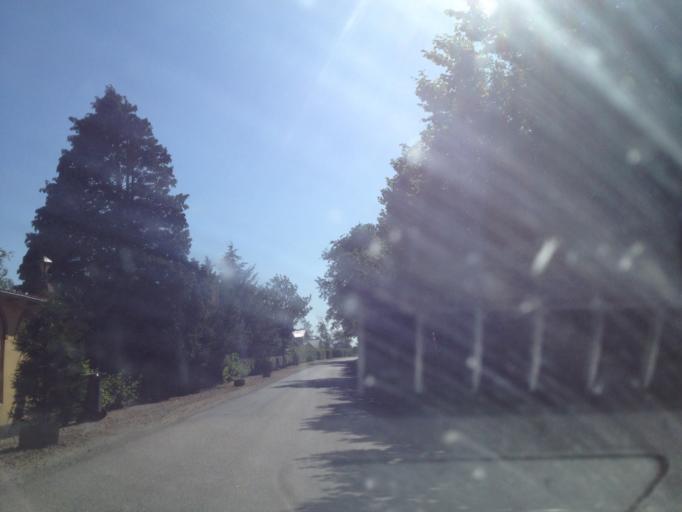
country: DK
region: South Denmark
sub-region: Kolding Kommune
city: Christiansfeld
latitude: 55.4040
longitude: 9.4977
